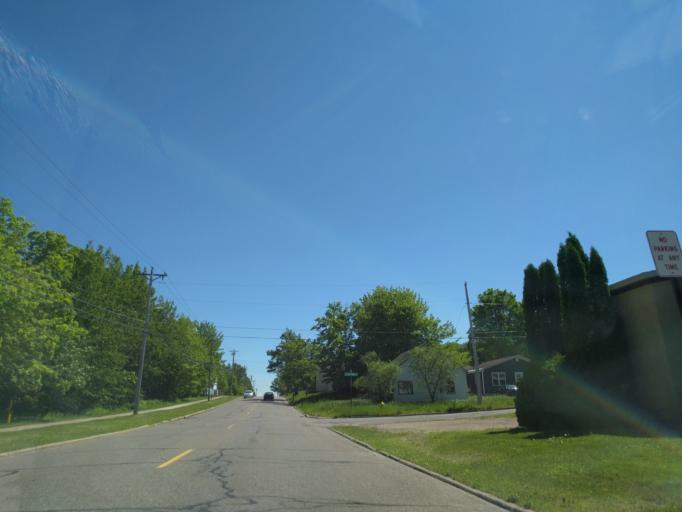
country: US
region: Michigan
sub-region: Marquette County
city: Marquette
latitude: 46.5513
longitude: -87.4123
